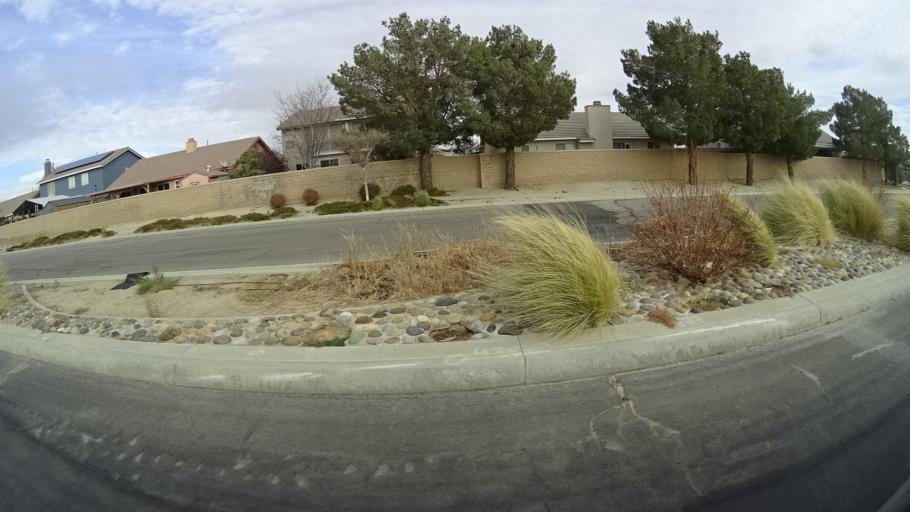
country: US
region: California
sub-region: Kern County
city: Rosamond
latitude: 34.8504
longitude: -118.1985
